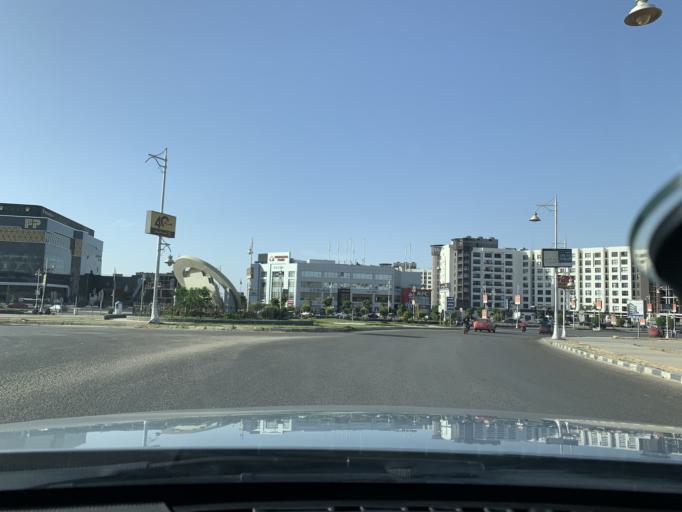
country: EG
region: Muhafazat al Qalyubiyah
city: Al Khankah
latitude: 30.0243
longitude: 31.4957
